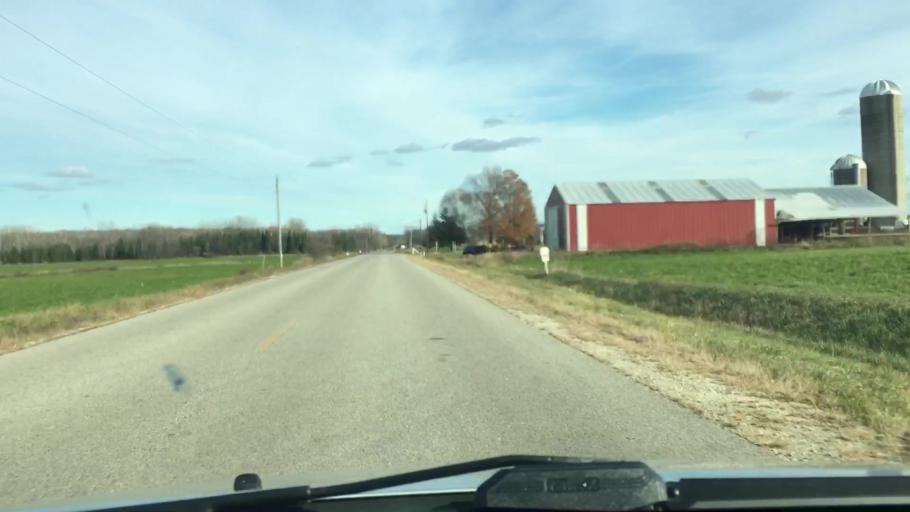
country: US
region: Wisconsin
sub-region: Kewaunee County
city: Algoma
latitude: 44.6902
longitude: -87.5694
